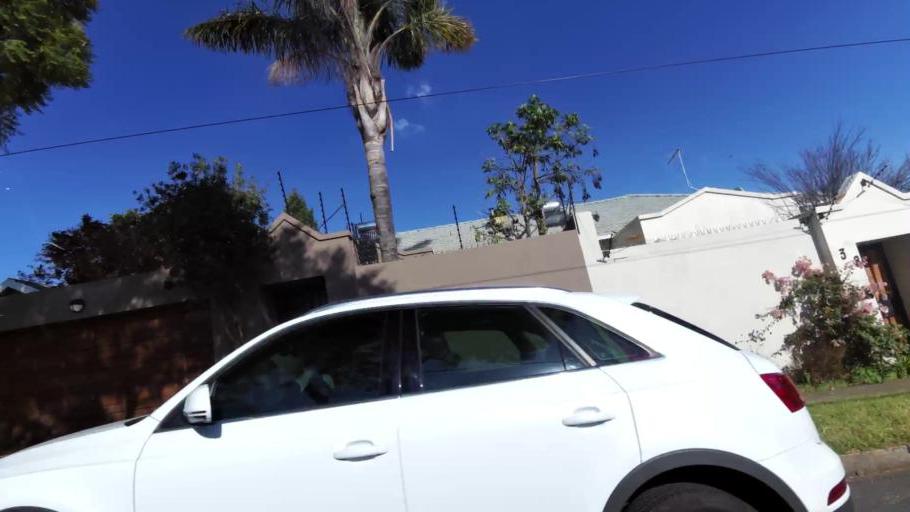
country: ZA
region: Gauteng
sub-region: City of Johannesburg Metropolitan Municipality
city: Johannesburg
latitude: -26.1777
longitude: 28.0025
